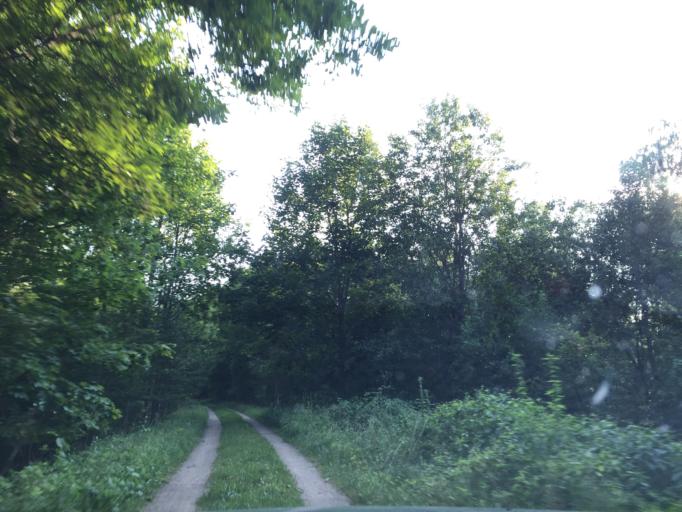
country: LV
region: Limbazu Rajons
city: Limbazi
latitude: 57.5641
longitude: 24.7884
